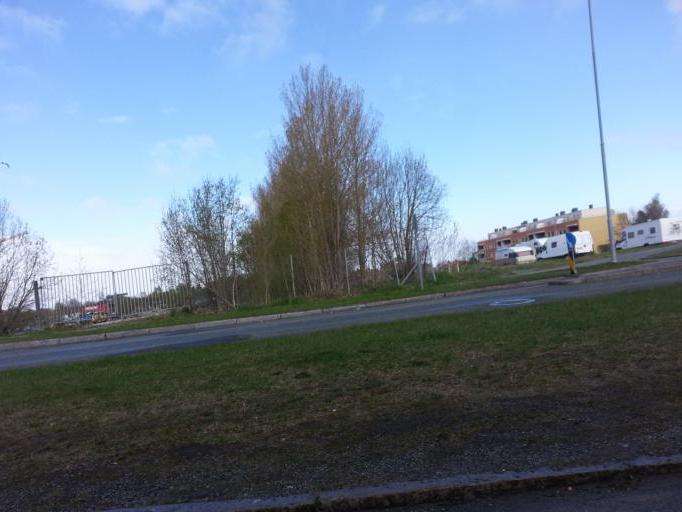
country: NO
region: Sor-Trondelag
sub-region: Trondheim
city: Trondheim
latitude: 63.3938
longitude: 10.3697
